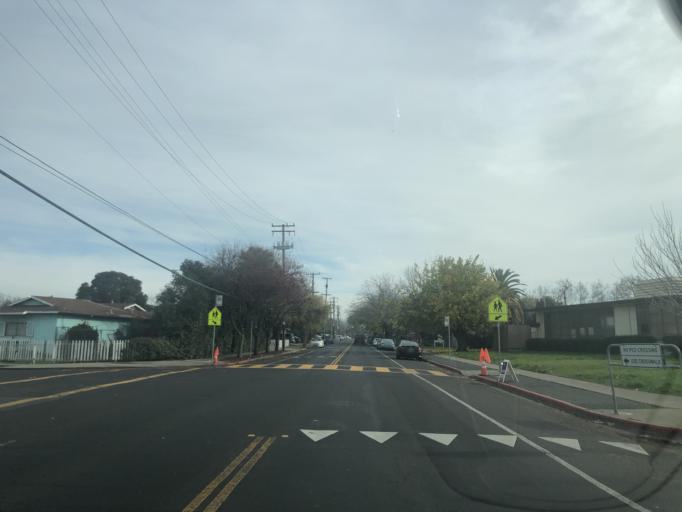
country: US
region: California
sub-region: Contra Costa County
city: Concord
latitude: 37.9962
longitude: -122.0347
